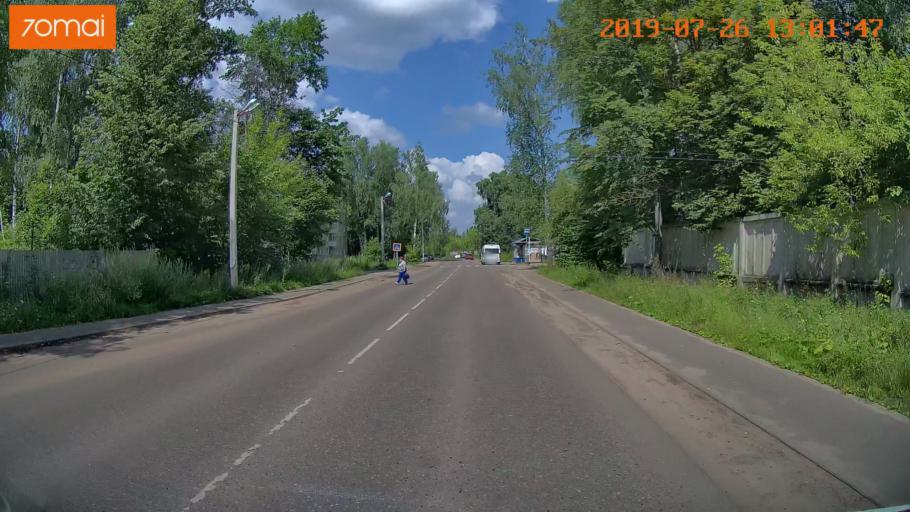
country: RU
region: Ivanovo
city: Bogorodskoye
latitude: 57.0404
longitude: 41.0123
